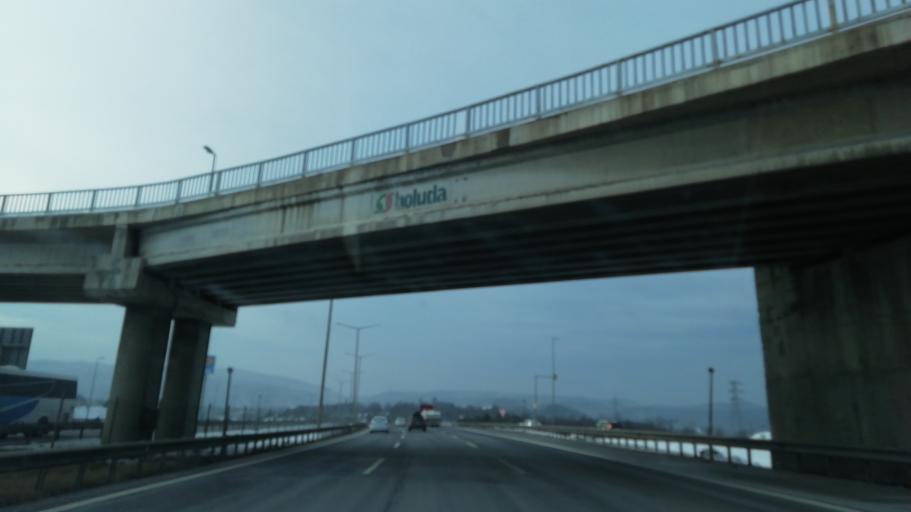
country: TR
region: Bolu
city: Bolu
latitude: 40.7251
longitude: 31.4628
